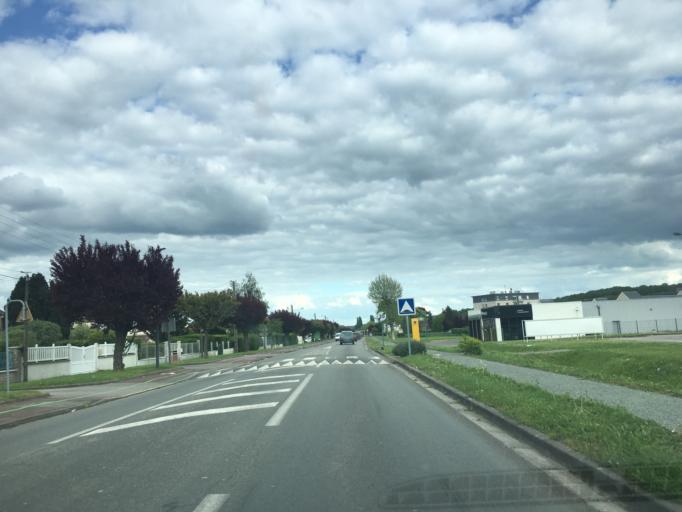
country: FR
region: Centre
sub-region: Departement d'Eure-et-Loir
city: Saint-Lubin-des-Joncherets
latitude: 48.7646
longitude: 1.2153
